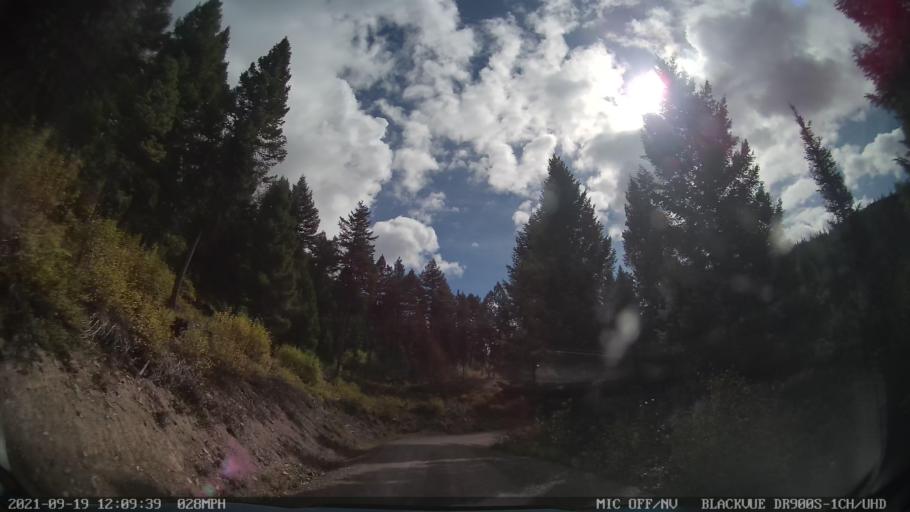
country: US
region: Montana
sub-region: Missoula County
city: Seeley Lake
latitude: 47.1824
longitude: -113.3894
